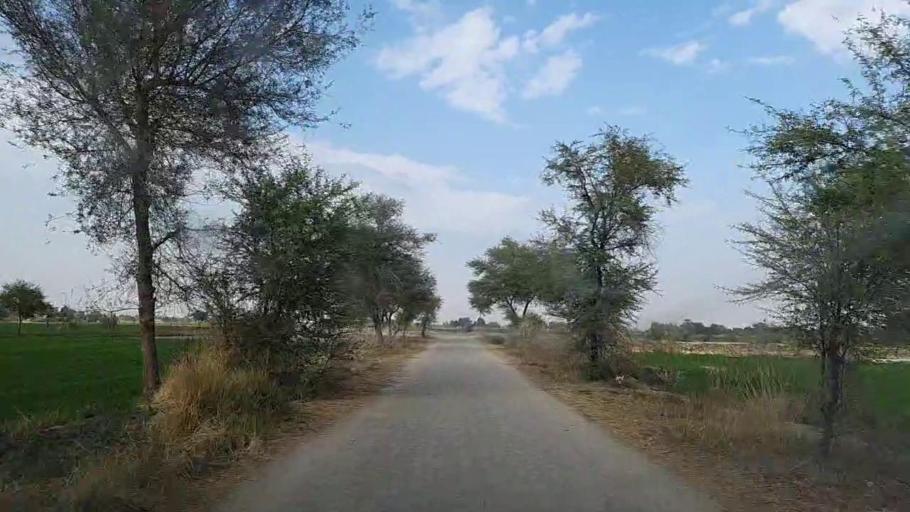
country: PK
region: Sindh
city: Sanghar
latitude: 26.2332
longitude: 69.0198
